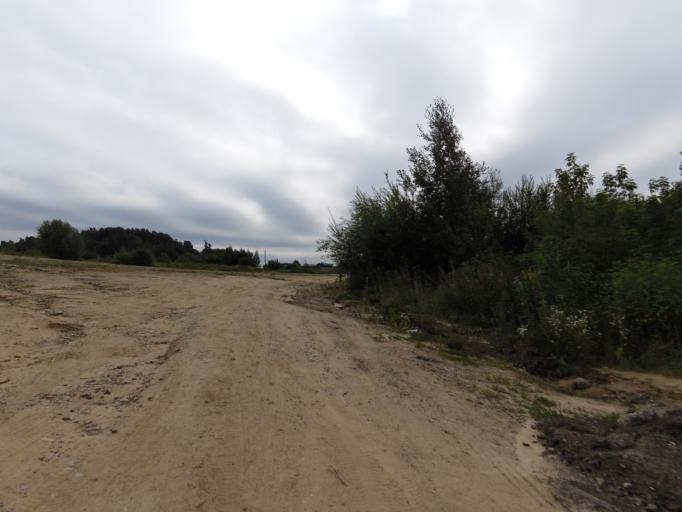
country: LT
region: Vilnius County
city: Rasos
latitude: 54.6579
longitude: 25.2902
